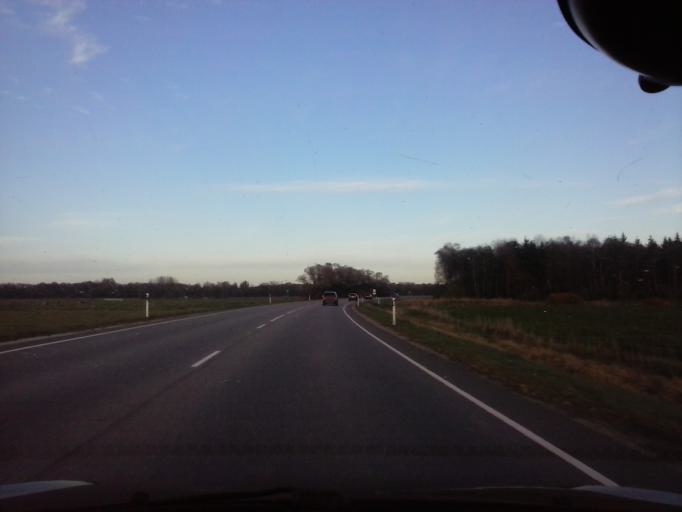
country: EE
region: Laeaene
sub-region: Ridala Parish
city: Uuemoisa
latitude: 58.9715
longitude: 23.8431
